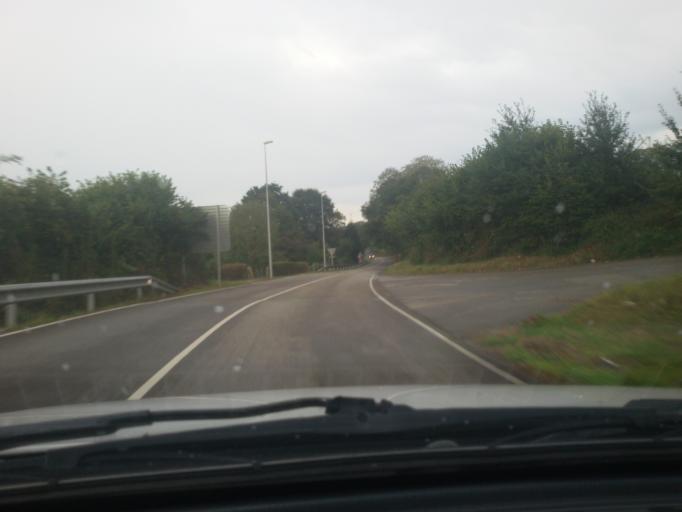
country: ES
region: Asturias
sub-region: Province of Asturias
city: Norena
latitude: 43.3739
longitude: -5.7216
